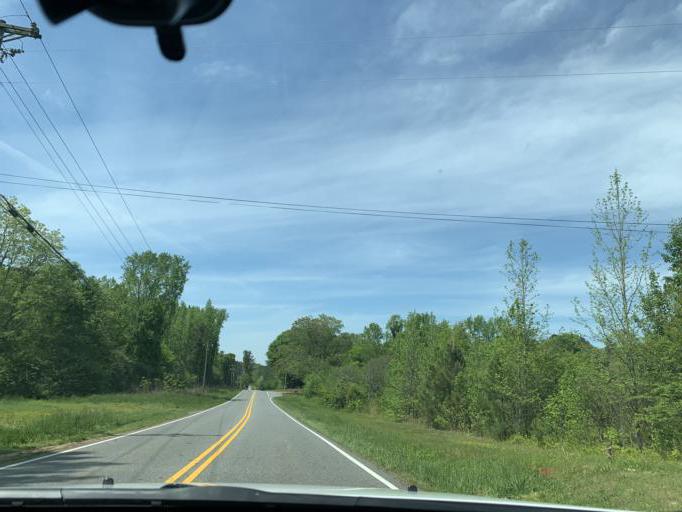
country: US
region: Georgia
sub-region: Forsyth County
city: Cumming
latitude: 34.2590
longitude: -84.1708
